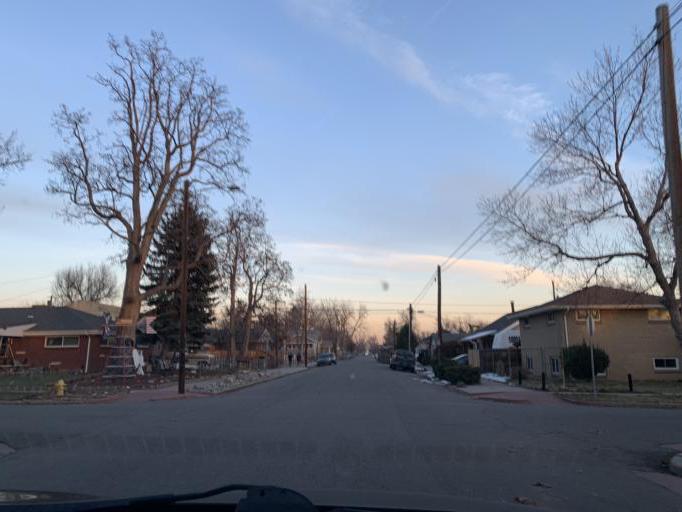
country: US
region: Colorado
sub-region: Adams County
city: Berkley
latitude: 39.7856
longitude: -105.0430
